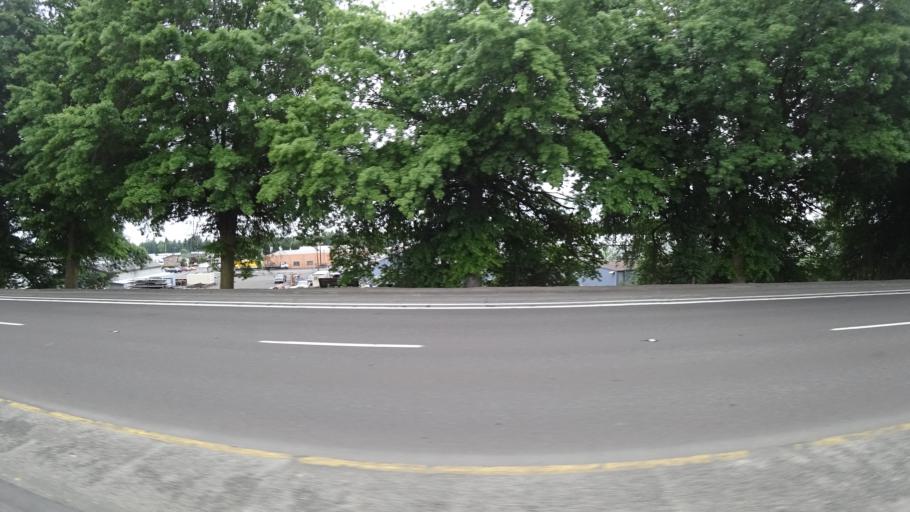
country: US
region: Washington
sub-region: Clark County
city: Vancouver
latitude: 45.5946
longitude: -122.6688
